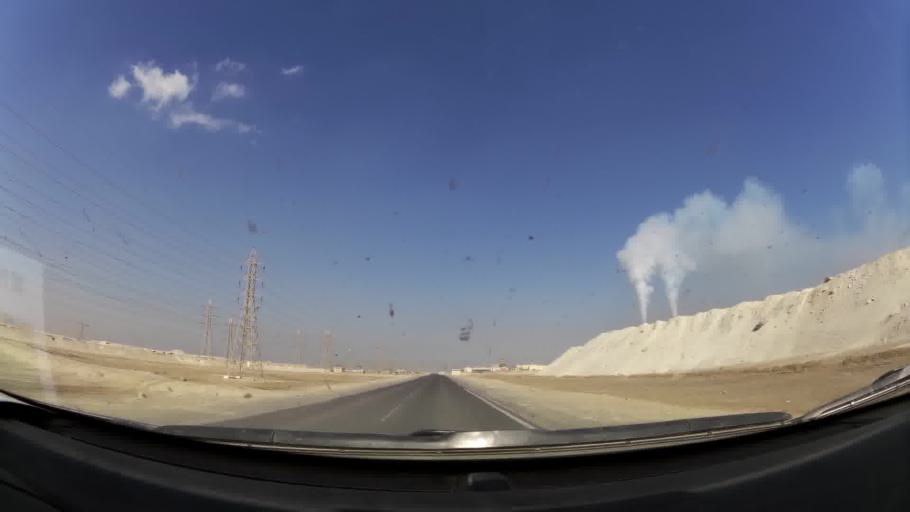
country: SA
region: Eastern Province
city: Al Khafji
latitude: 28.6915
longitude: 48.3572
